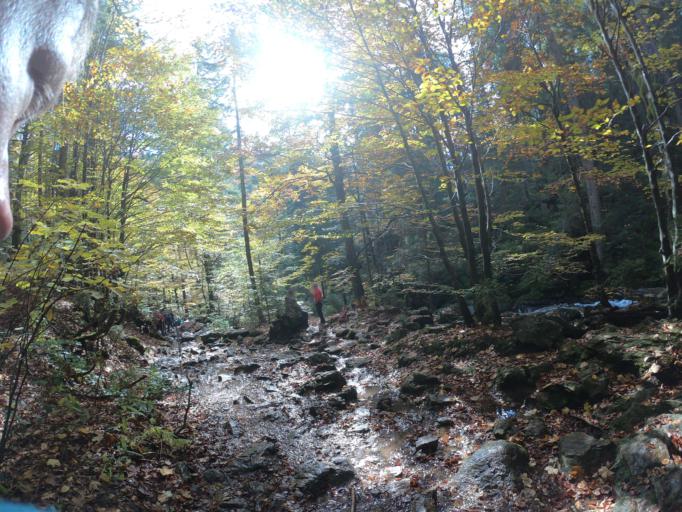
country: DE
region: Bavaria
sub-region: Lower Bavaria
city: Bodenmais
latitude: 49.0892
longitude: 13.1192
